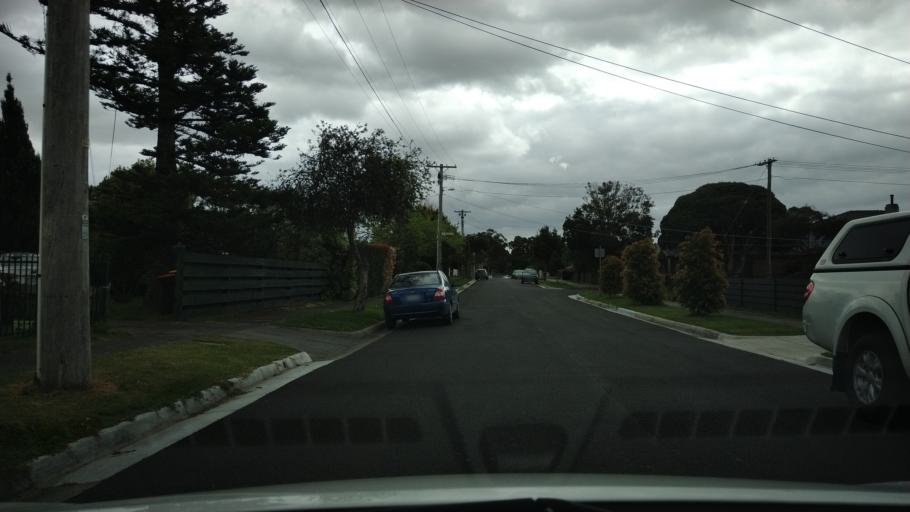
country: AU
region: Victoria
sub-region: Greater Dandenong
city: Noble Park
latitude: -37.9734
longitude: 145.1801
